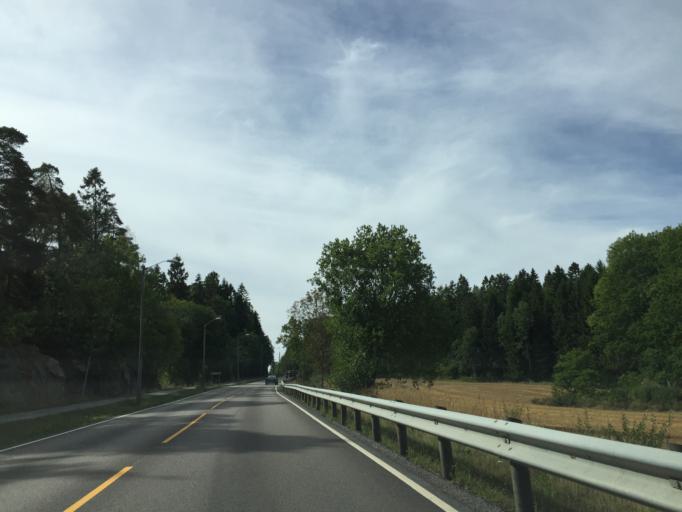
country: NO
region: Ostfold
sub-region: Fredrikstad
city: Fredrikstad
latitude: 59.1893
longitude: 10.9348
